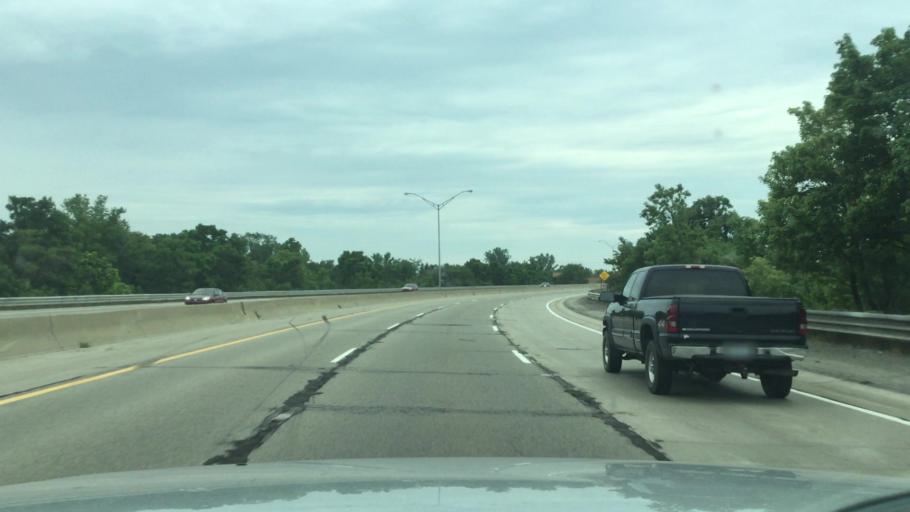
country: US
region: Michigan
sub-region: Genesee County
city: Flint
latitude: 42.9975
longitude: -83.6755
